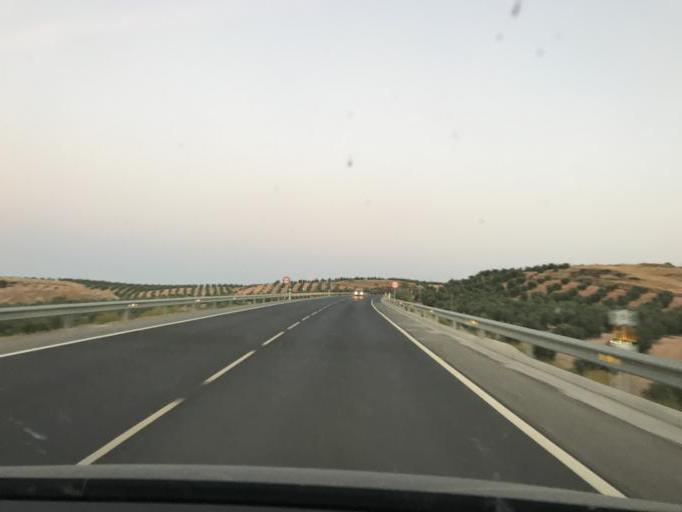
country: ES
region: Andalusia
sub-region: Provincia de Jaen
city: Guadahortuna
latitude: 37.5483
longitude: -3.3899
